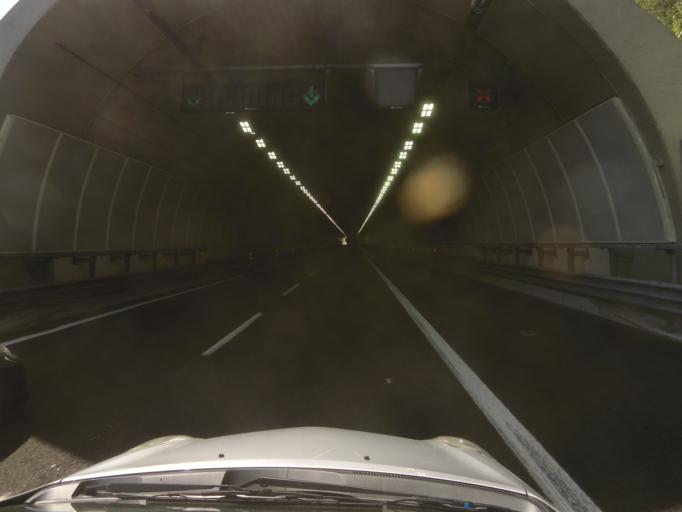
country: IT
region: Emilia-Romagna
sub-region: Provincia di Bologna
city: Marzabotto
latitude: 44.2906
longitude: 11.2083
